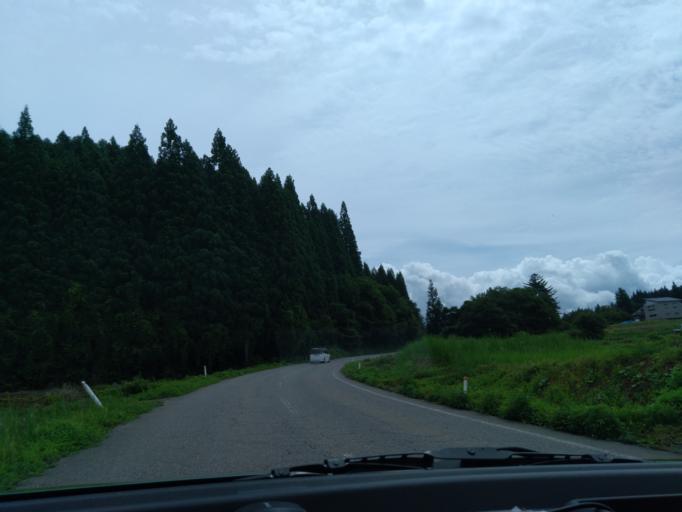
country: JP
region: Akita
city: Kakunodatemachi
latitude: 39.5811
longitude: 140.6245
